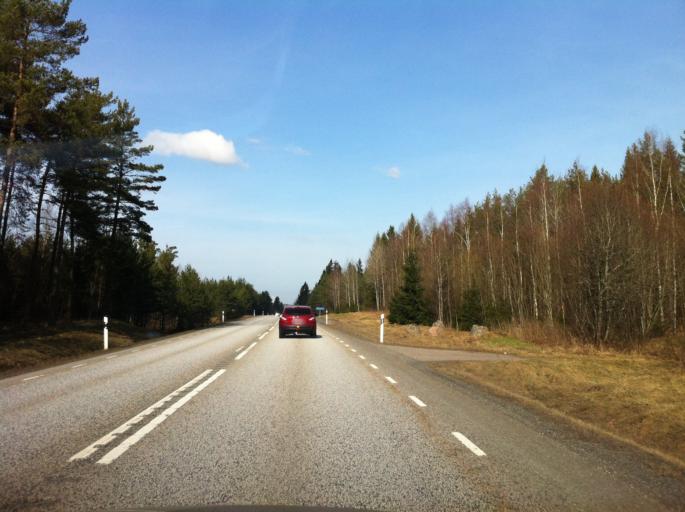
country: SE
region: Joenkoeping
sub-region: Mullsjo Kommun
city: Mullsjoe
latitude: 57.9593
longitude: 13.8319
